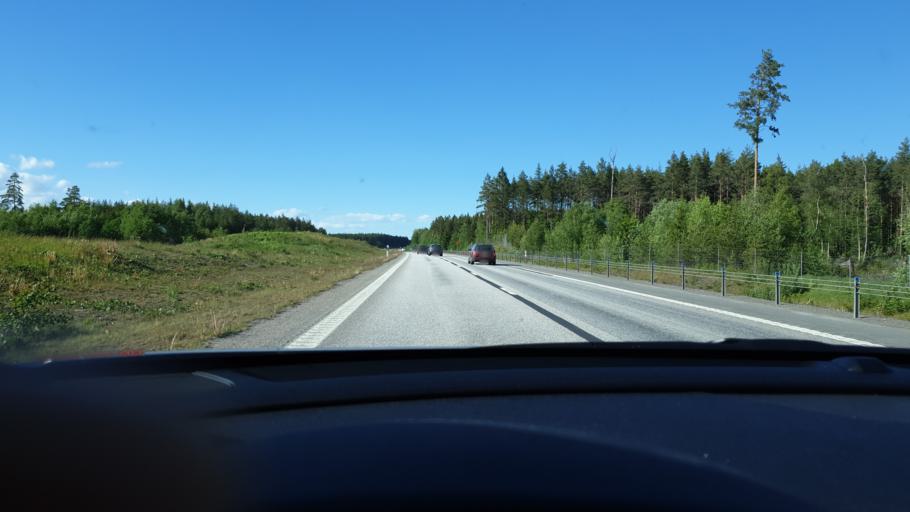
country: SE
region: Uppsala
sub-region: Tierps Kommun
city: Tierp
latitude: 60.2685
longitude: 17.5014
